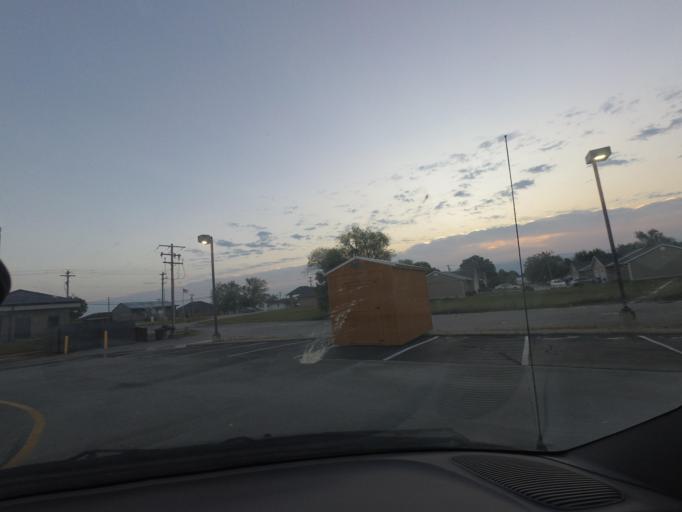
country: US
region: Missouri
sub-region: Macon County
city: Macon
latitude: 39.7514
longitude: -92.4670
